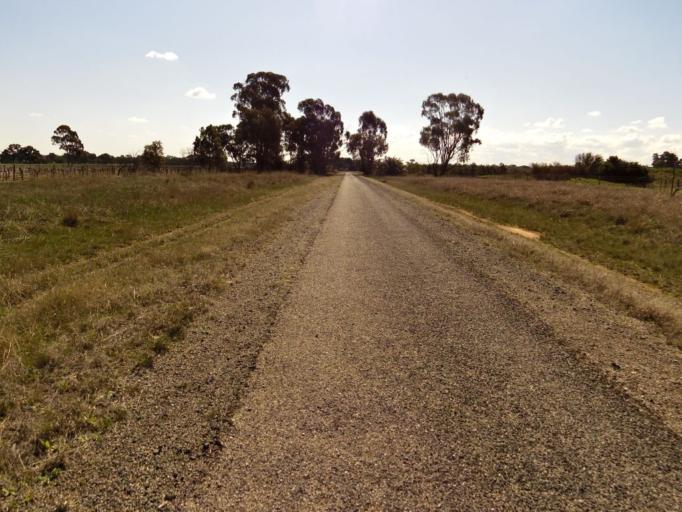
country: AU
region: New South Wales
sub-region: Corowa Shire
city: Corowa
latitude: -36.0417
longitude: 146.4547
